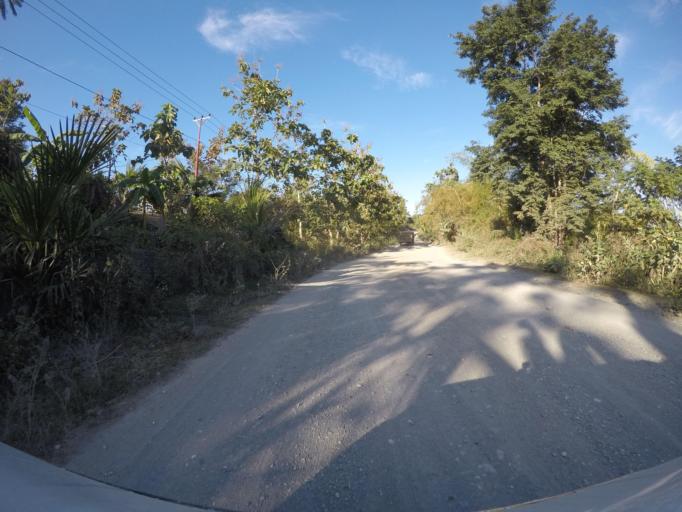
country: TL
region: Viqueque
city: Viqueque
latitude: -8.8671
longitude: 126.3323
